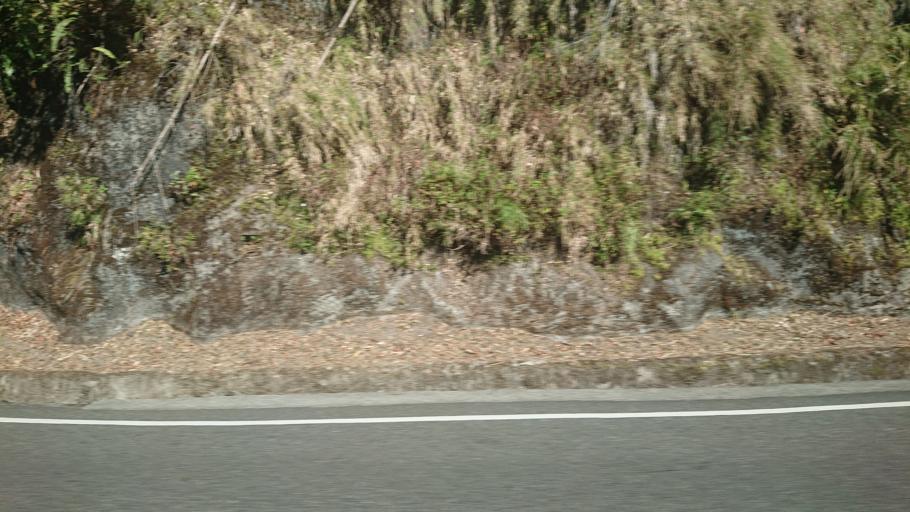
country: TW
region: Taiwan
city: Lugu
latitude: 23.4758
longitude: 120.7343
